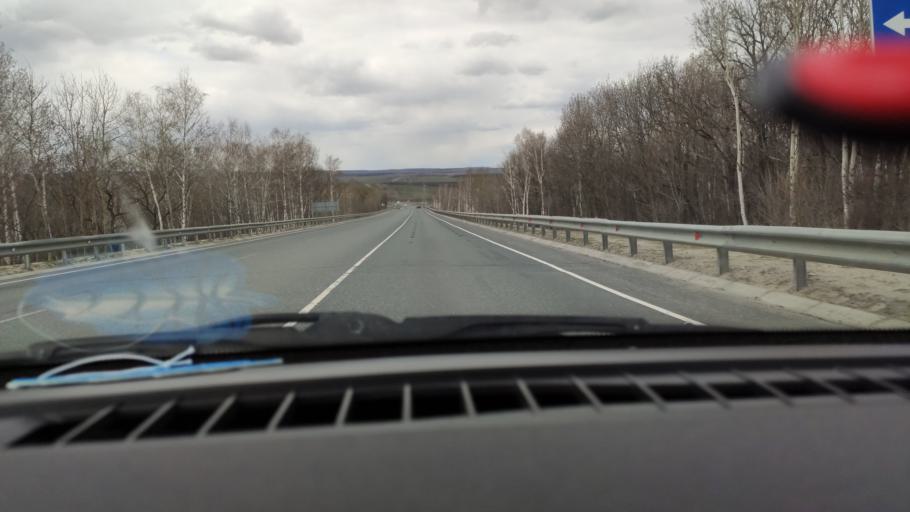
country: RU
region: Saratov
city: Vol'sk
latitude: 52.1141
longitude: 47.3091
